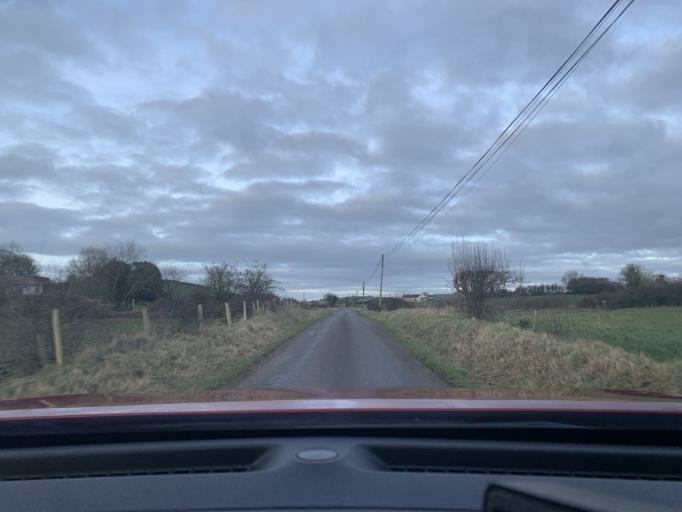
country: IE
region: Connaught
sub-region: Sligo
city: Ballymote
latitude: 54.0499
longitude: -8.5707
